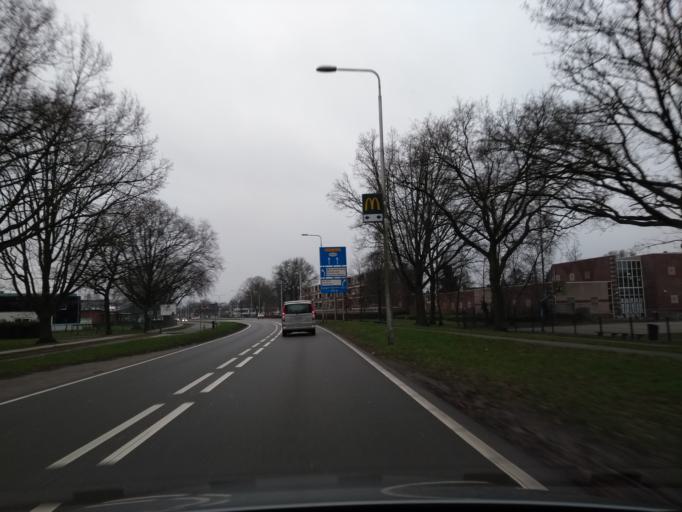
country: NL
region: Overijssel
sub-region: Gemeente Almelo
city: Almelo
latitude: 52.3521
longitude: 6.6758
